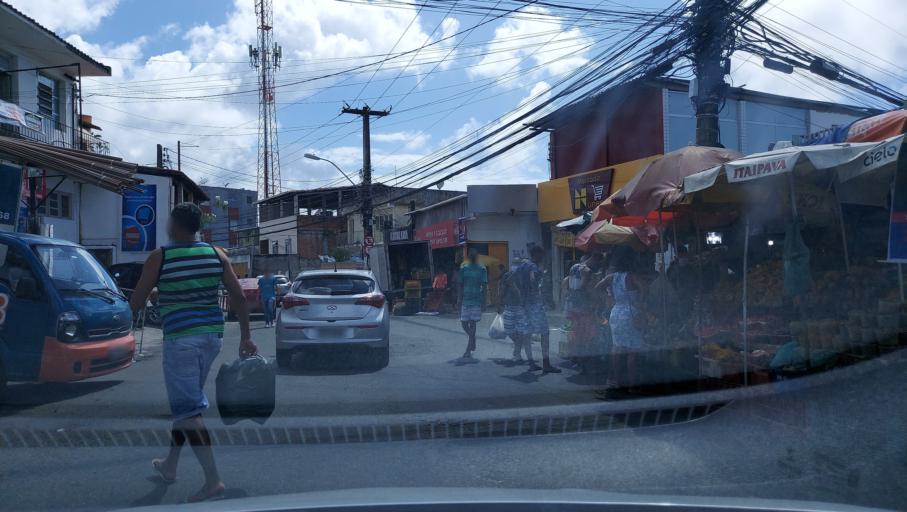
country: BR
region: Bahia
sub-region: Salvador
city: Salvador
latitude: -12.9881
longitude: -38.4784
